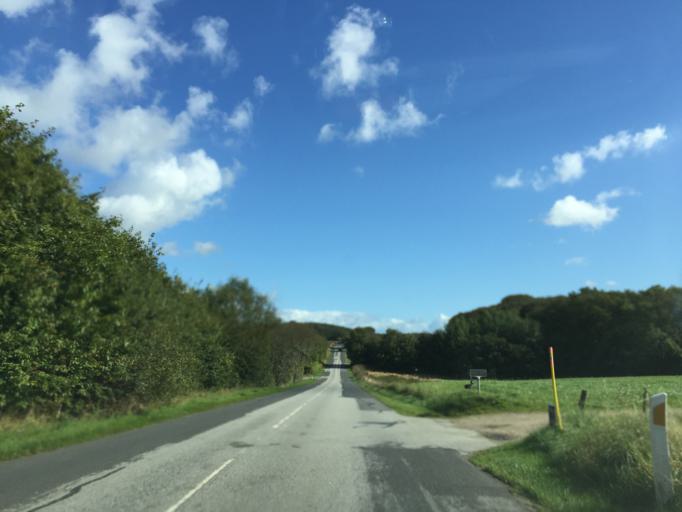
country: DK
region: Central Jutland
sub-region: Viborg Kommune
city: Viborg
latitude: 56.4419
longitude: 9.4929
